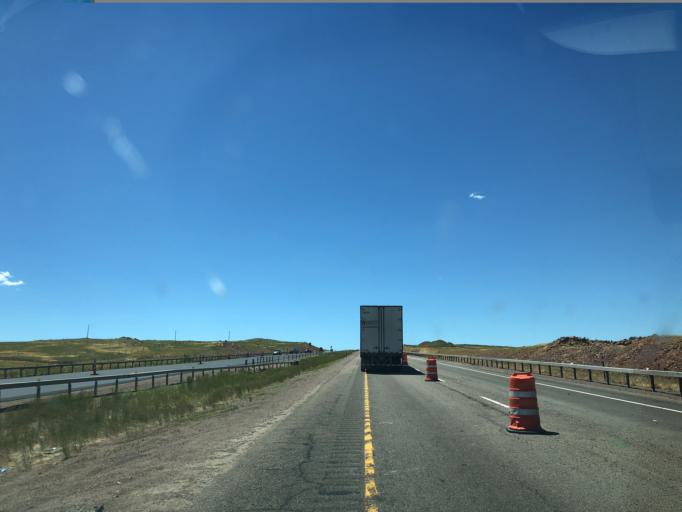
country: US
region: Wyoming
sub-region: Laramie County
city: Cheyenne
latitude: 41.0974
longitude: -105.1721
